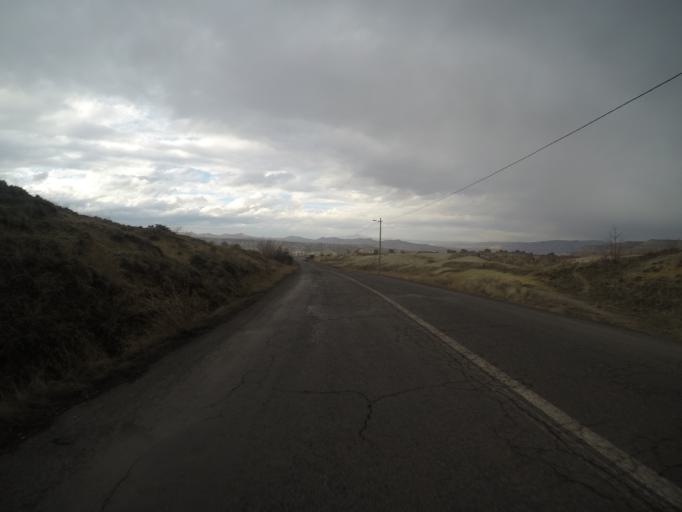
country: TR
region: Nevsehir
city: Goereme
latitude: 38.6381
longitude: 34.8511
